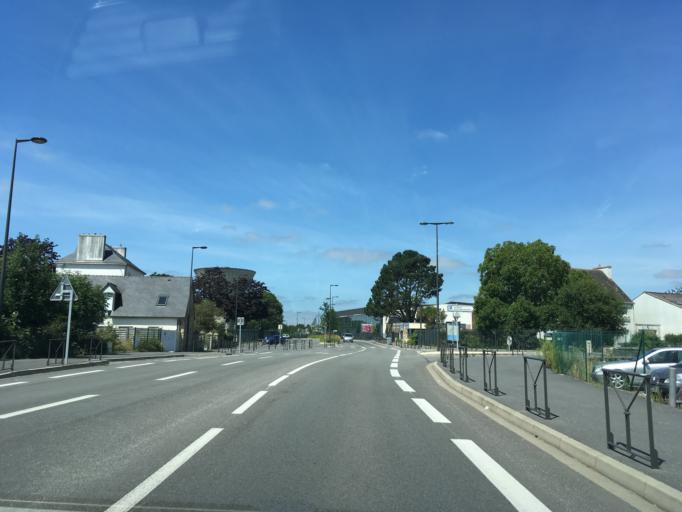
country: FR
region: Brittany
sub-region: Departement du Finistere
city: Quimper
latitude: 48.0105
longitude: -4.0965
